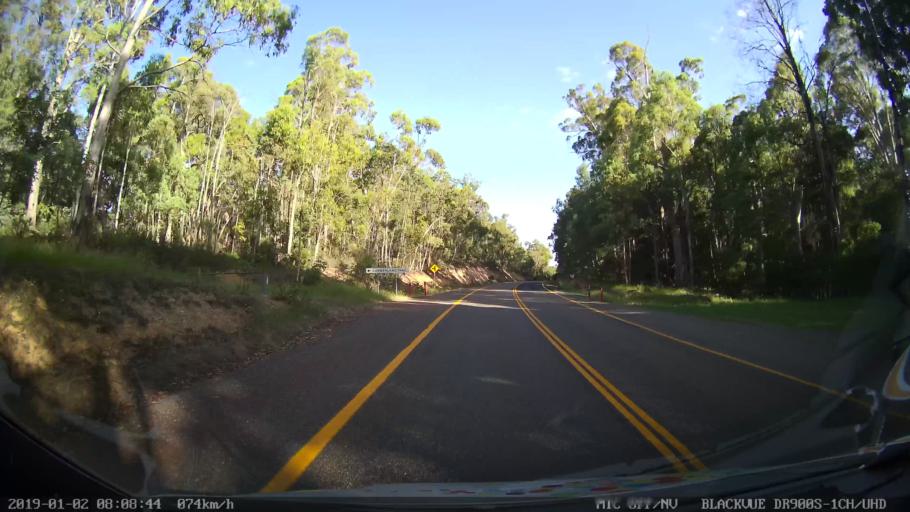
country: AU
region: New South Wales
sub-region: Tumut Shire
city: Tumut
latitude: -35.6140
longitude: 148.3826
